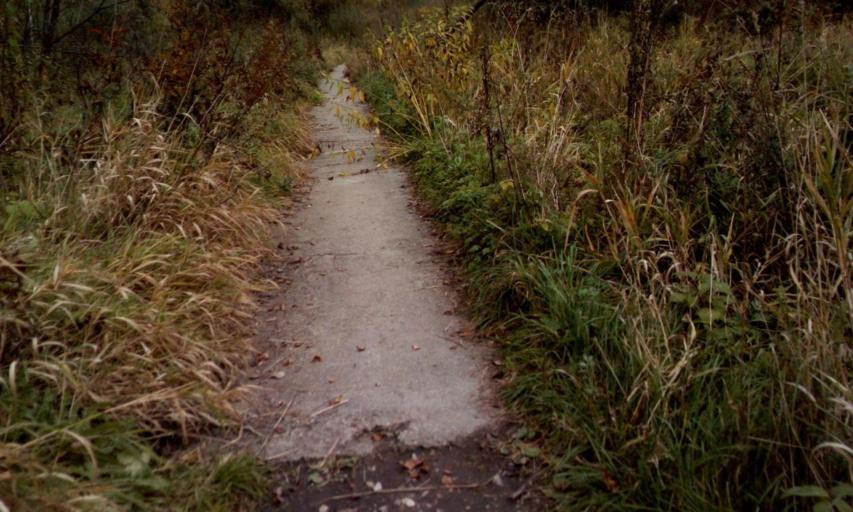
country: RU
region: Moskovskaya
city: Lesnoy Gorodok
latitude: 55.6863
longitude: 37.2164
